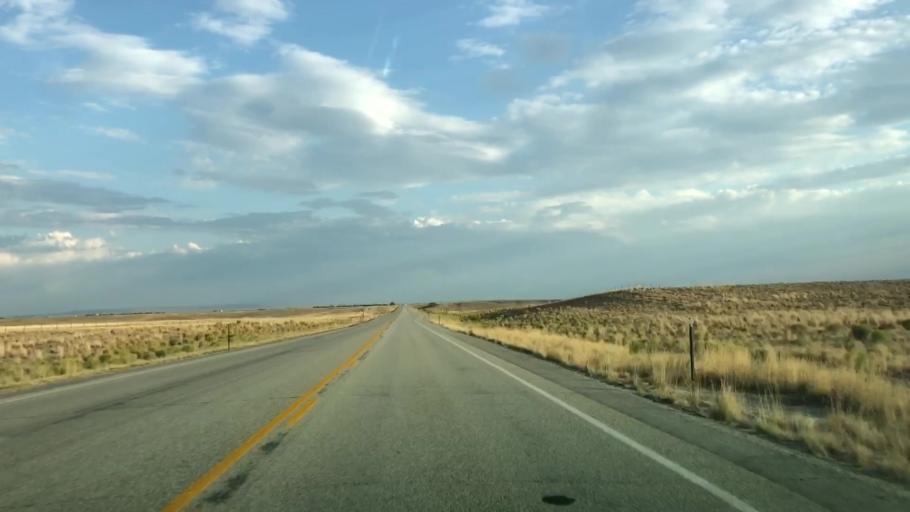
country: US
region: Wyoming
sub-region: Sweetwater County
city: North Rock Springs
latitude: 42.1867
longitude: -109.4793
